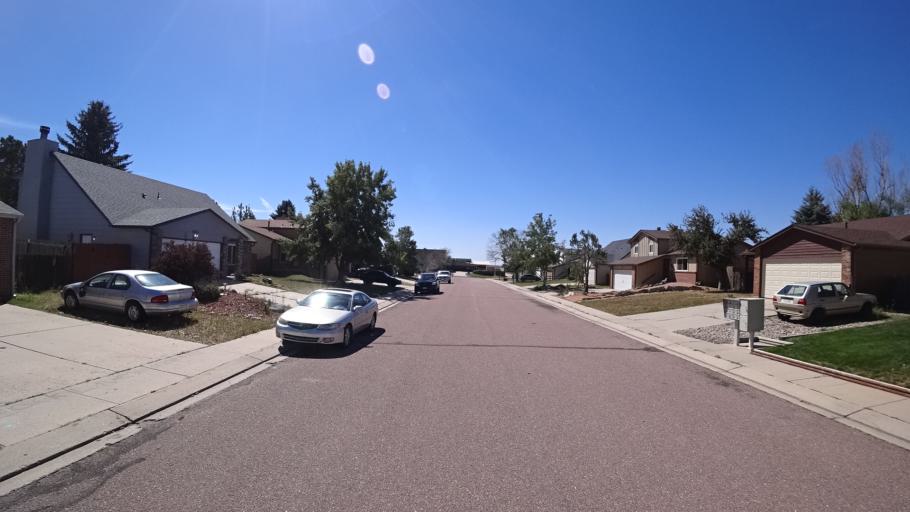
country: US
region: Colorado
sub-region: El Paso County
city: Black Forest
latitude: 38.9487
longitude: -104.7561
